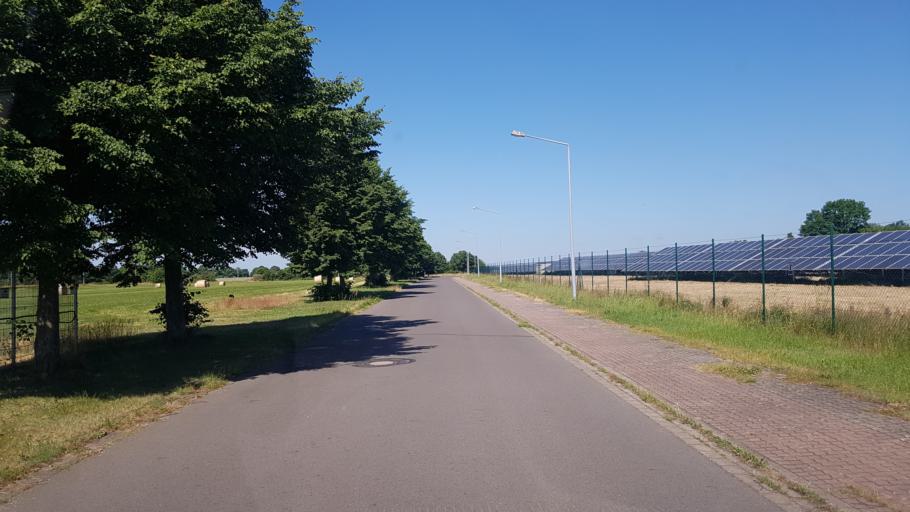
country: DE
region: Brandenburg
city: Plessa
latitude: 51.4682
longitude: 13.6033
